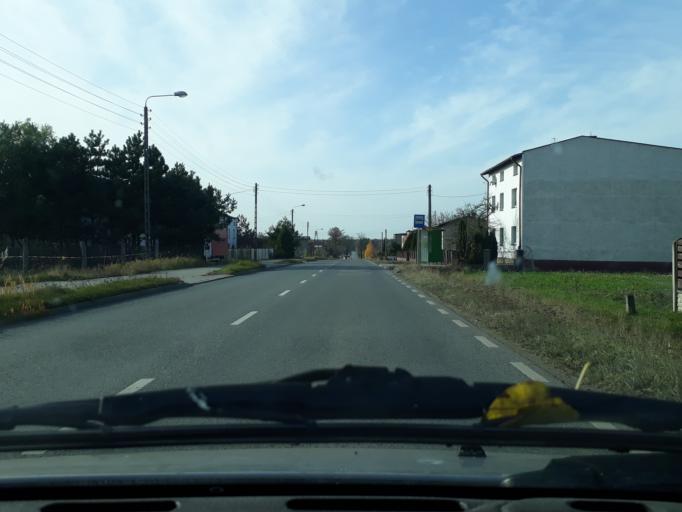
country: PL
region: Silesian Voivodeship
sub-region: Powiat lubliniecki
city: Psary
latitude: 50.5768
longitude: 18.9906
